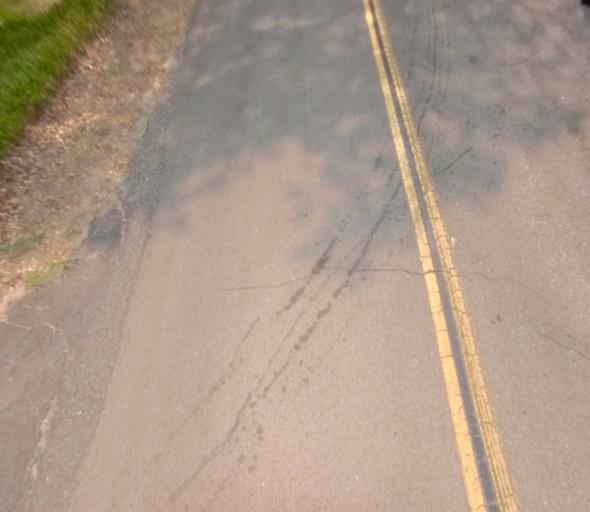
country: US
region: California
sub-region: Madera County
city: Oakhurst
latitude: 37.3052
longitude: -119.6159
